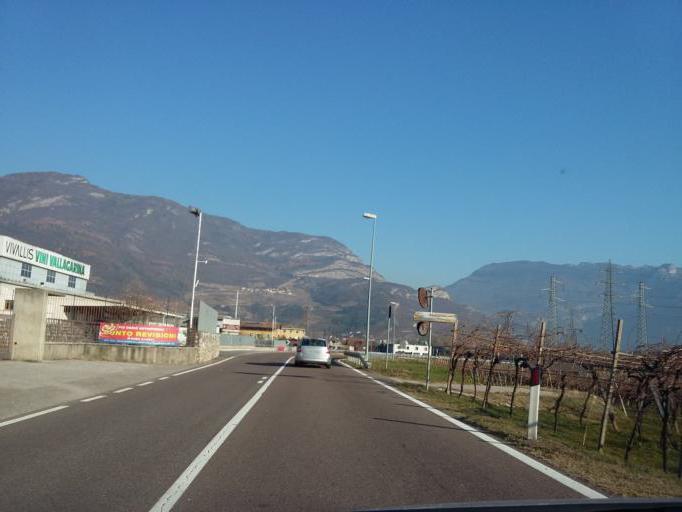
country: IT
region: Trentino-Alto Adige
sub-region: Provincia di Trento
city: Nogaredo
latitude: 45.9096
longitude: 11.0296
